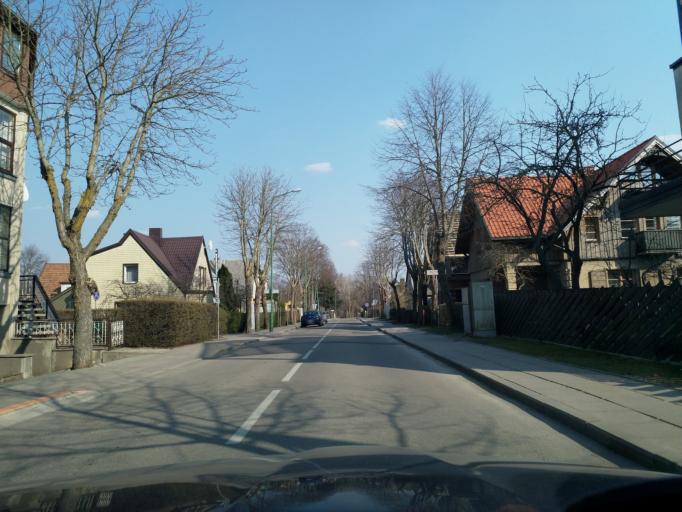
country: LT
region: Klaipedos apskritis
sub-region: Klaipeda
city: Palanga
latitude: 55.9119
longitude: 21.0695
